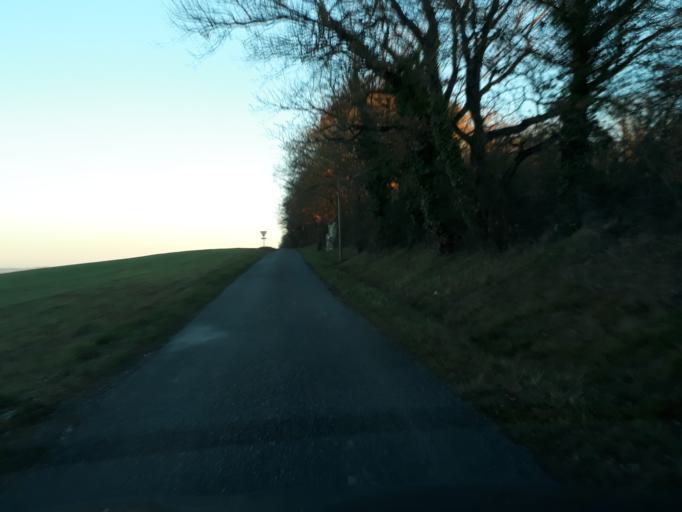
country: FR
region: Midi-Pyrenees
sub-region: Departement du Gers
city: Pavie
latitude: 43.6087
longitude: 0.6832
